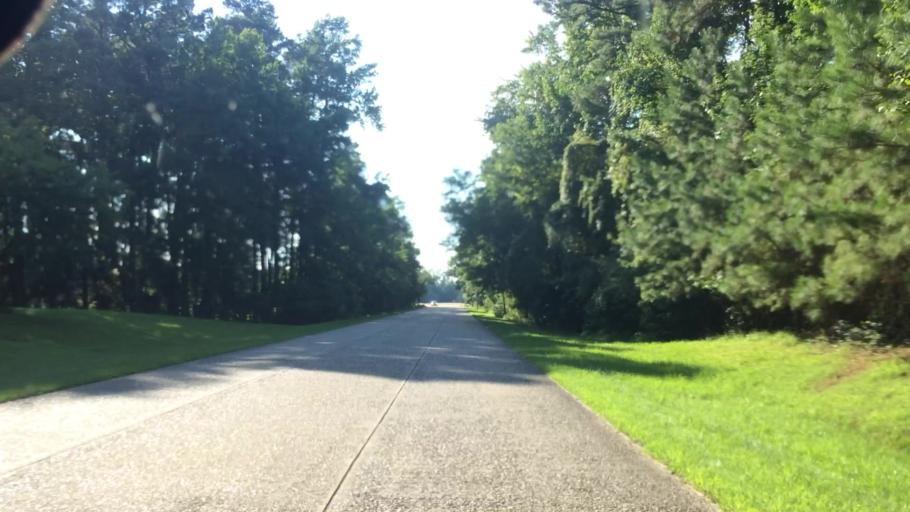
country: US
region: Virginia
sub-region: James City County
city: Williamsburg
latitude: 37.2222
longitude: -76.7747
